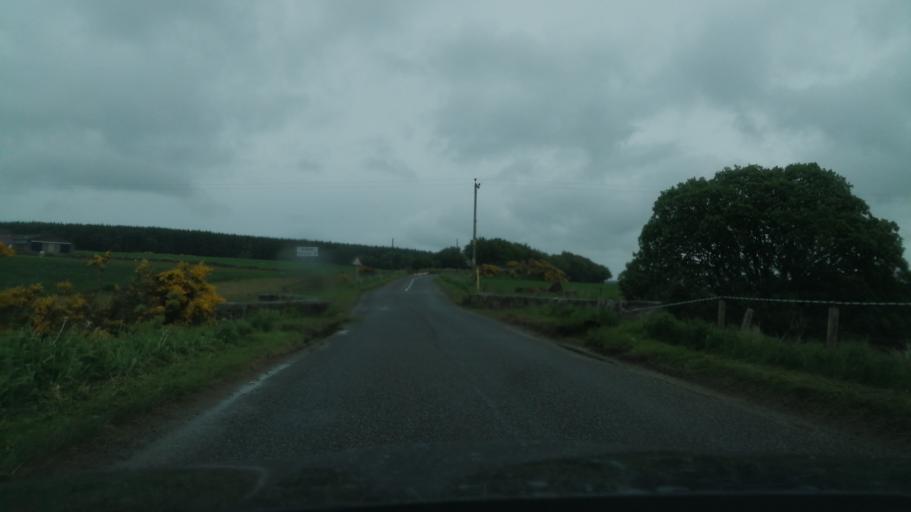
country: GB
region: Scotland
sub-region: Aberdeenshire
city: Portsoy
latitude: 57.5988
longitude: -2.7305
